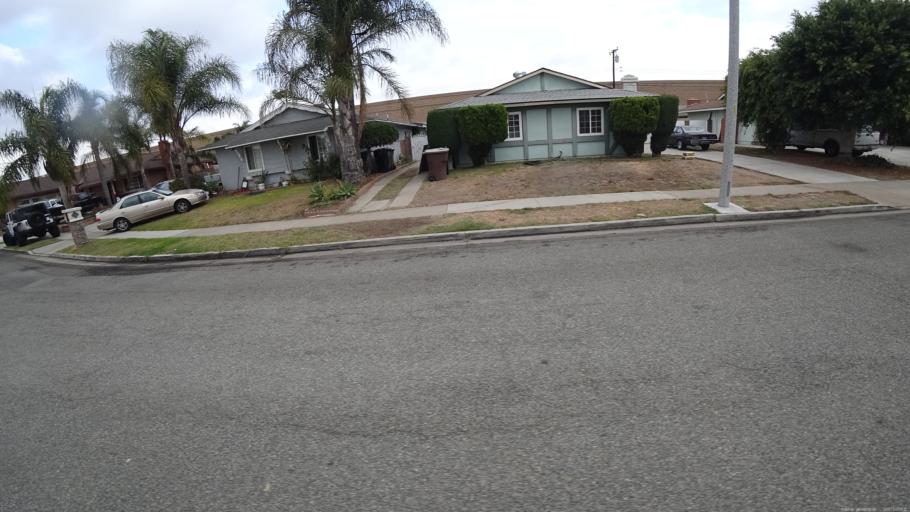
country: US
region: California
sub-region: Orange County
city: Garden Grove
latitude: 33.7651
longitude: -117.9627
